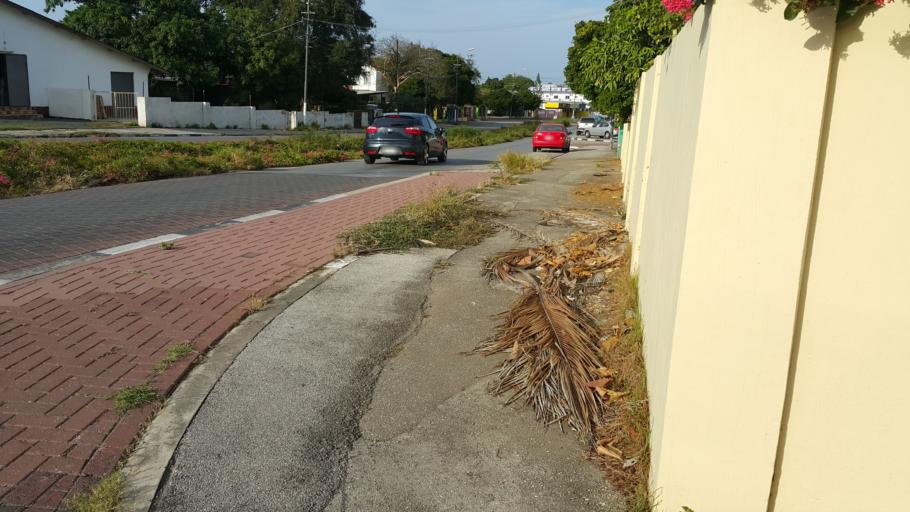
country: CW
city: Willemstad
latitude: 12.1467
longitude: -68.9250
